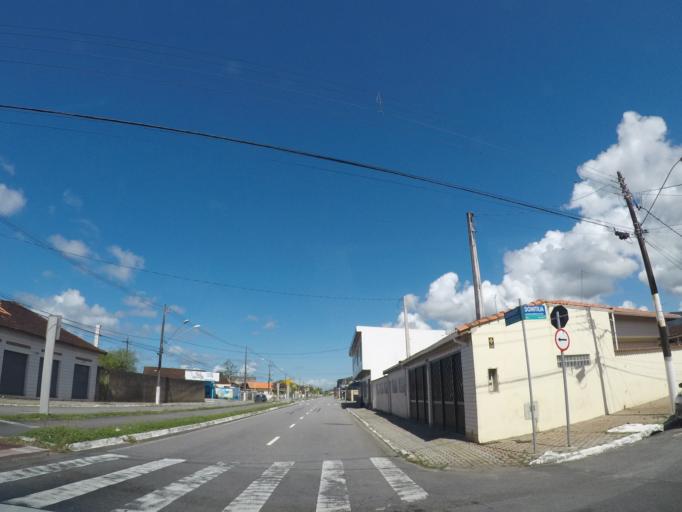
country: BR
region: Sao Paulo
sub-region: Mongagua
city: Mongagua
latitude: -24.0564
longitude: -46.5501
